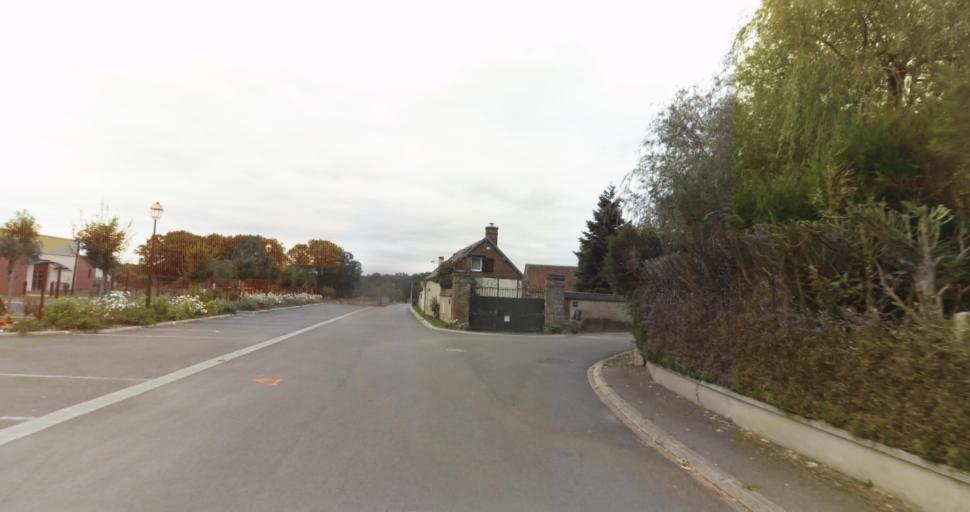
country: FR
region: Centre
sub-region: Departement d'Eure-et-Loir
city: Sorel-Moussel
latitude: 48.8637
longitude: 1.3480
